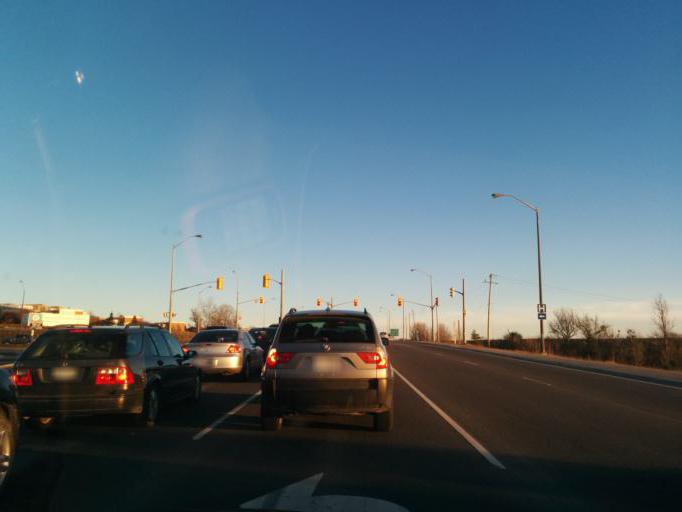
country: CA
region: Ontario
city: Orangeville
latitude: 43.9196
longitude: -80.0781
